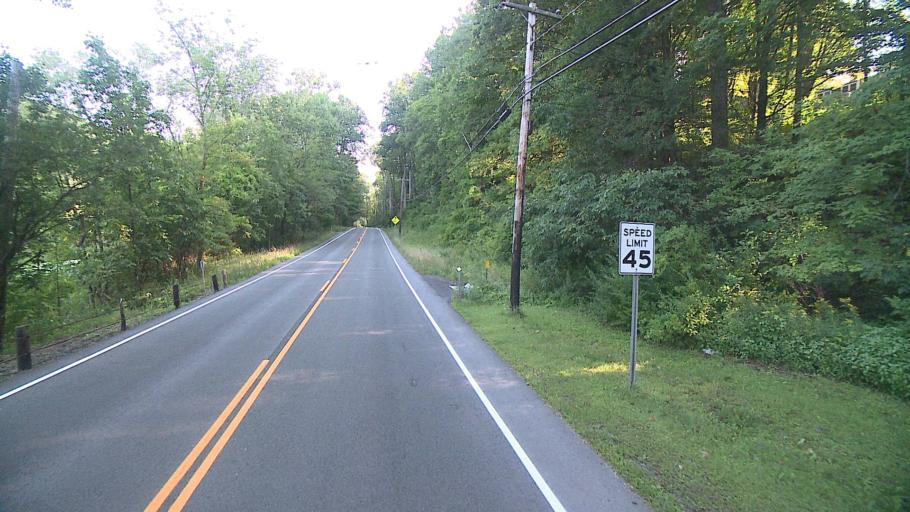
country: US
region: Connecticut
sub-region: Litchfield County
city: Kent
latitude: 41.6806
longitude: -73.5065
